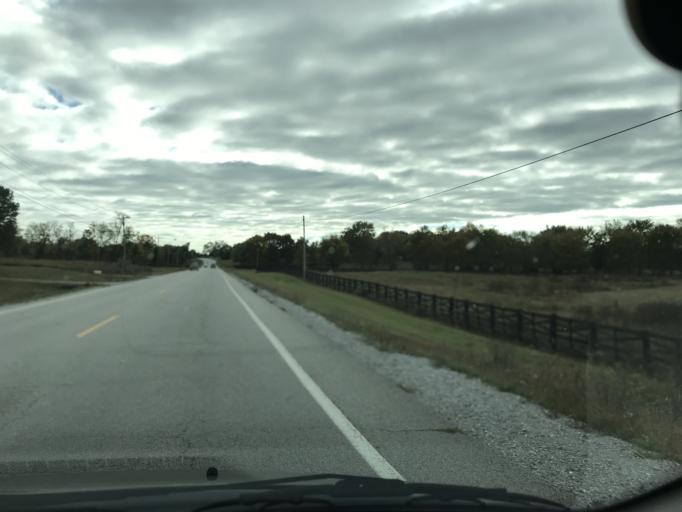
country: US
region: Tennessee
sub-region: Hamilton County
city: Collegedale
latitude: 35.1549
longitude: -85.0390
